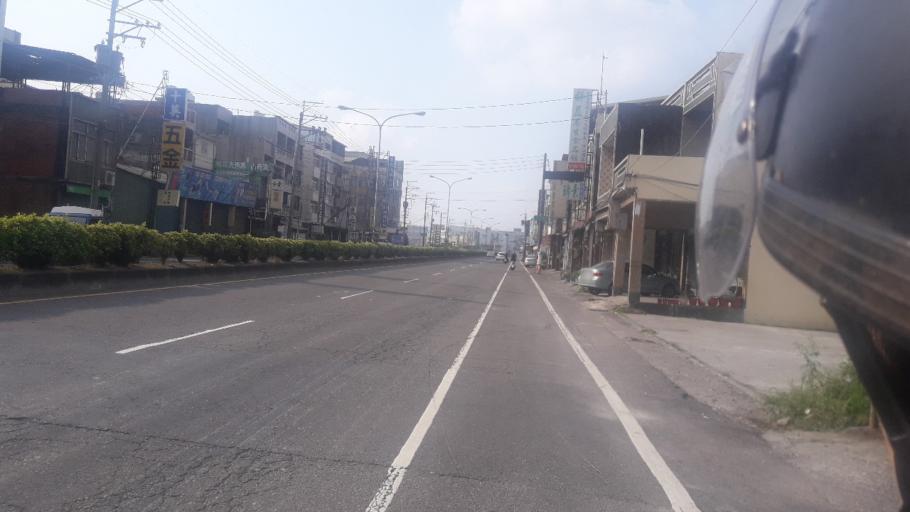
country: TW
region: Taiwan
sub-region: Tainan
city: Tainan
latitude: 22.8625
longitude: 120.2583
